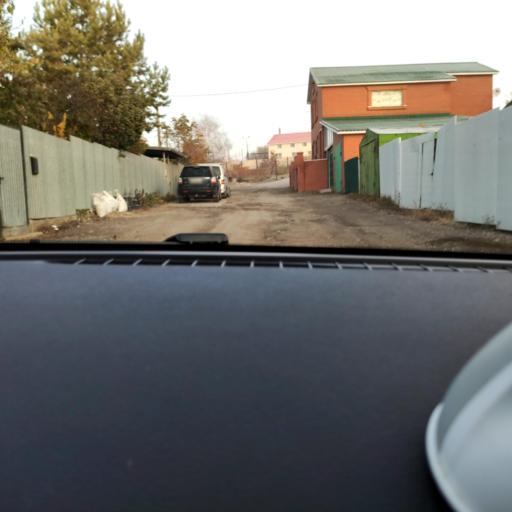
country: RU
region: Samara
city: Samara
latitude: 53.1787
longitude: 50.1818
